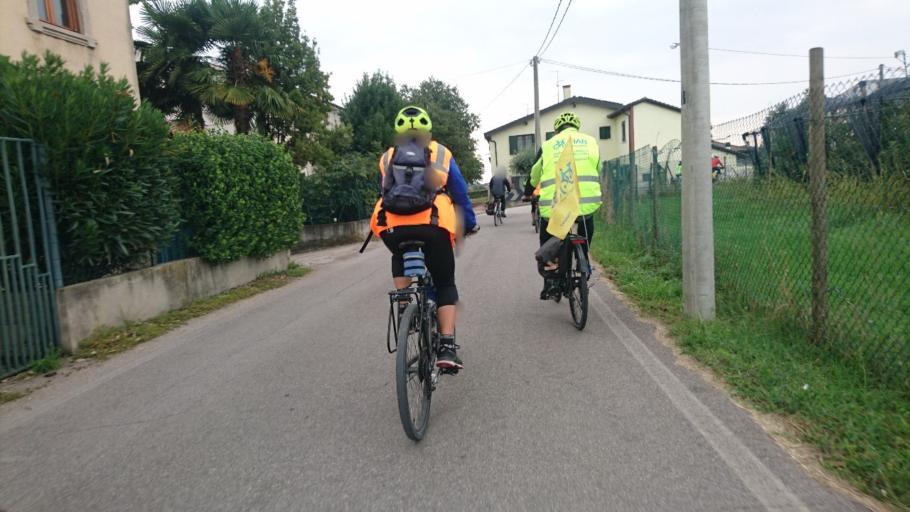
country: IT
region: Veneto
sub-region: Provincia di Verona
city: San Martino Buon Albergo
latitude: 45.4166
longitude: 11.0571
